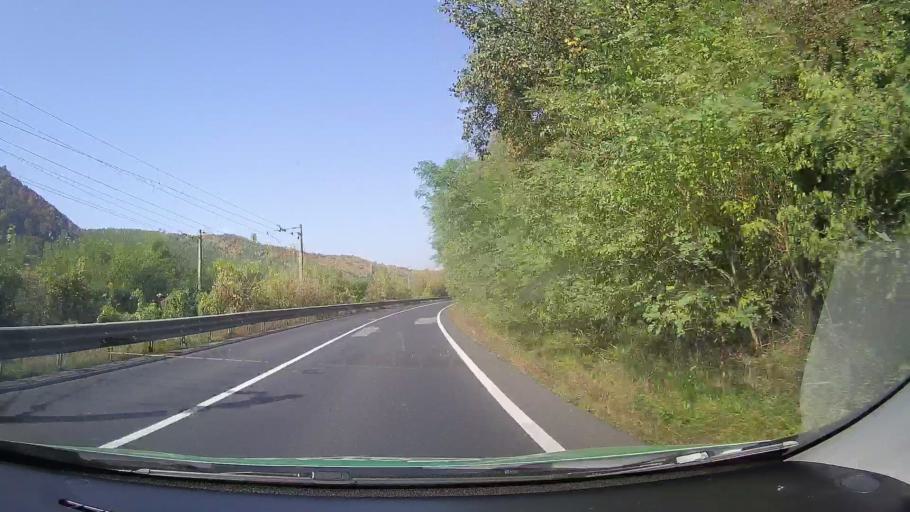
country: RO
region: Hunedoara
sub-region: Comuna Zam
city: Zam
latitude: 45.9756
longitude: 22.4333
